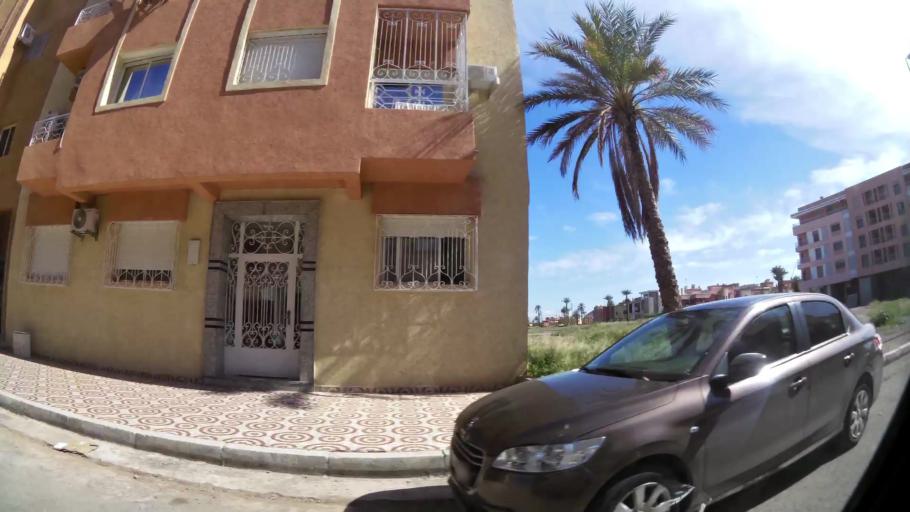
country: MA
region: Marrakech-Tensift-Al Haouz
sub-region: Marrakech
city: Marrakesh
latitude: 31.6659
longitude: -8.0251
